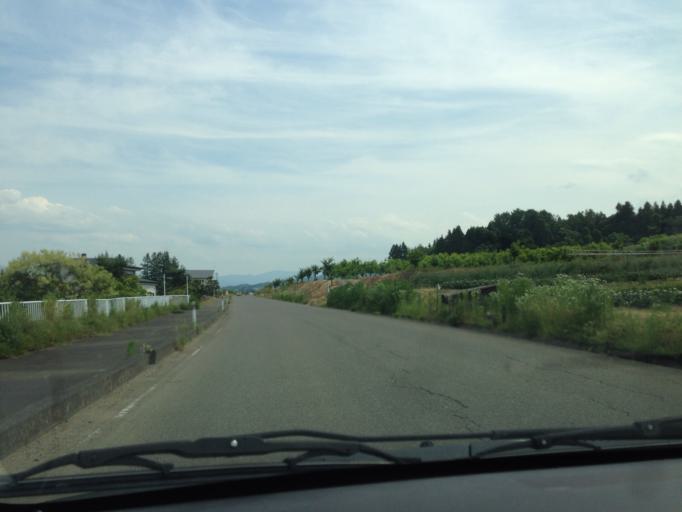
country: JP
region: Fukushima
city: Kitakata
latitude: 37.5554
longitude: 139.7988
